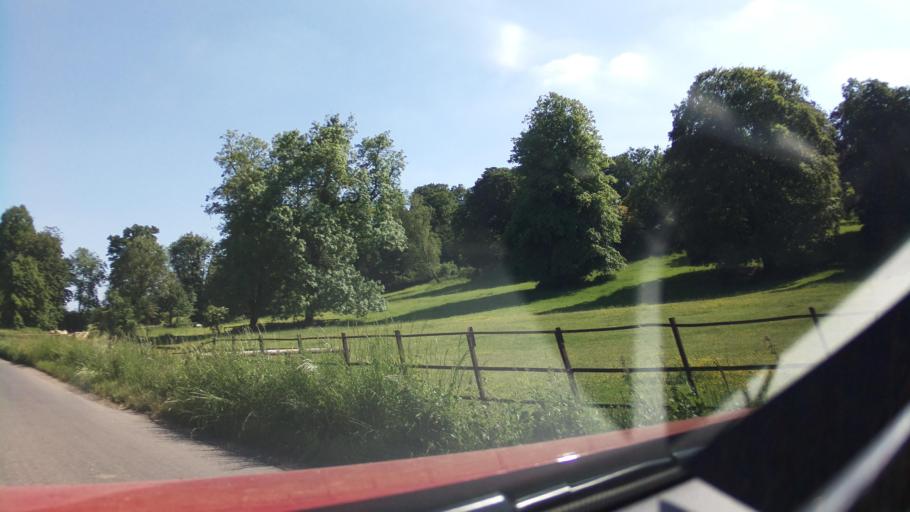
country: GB
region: England
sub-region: Hampshire
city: Abbotts Ann
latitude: 51.2556
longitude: -1.5787
